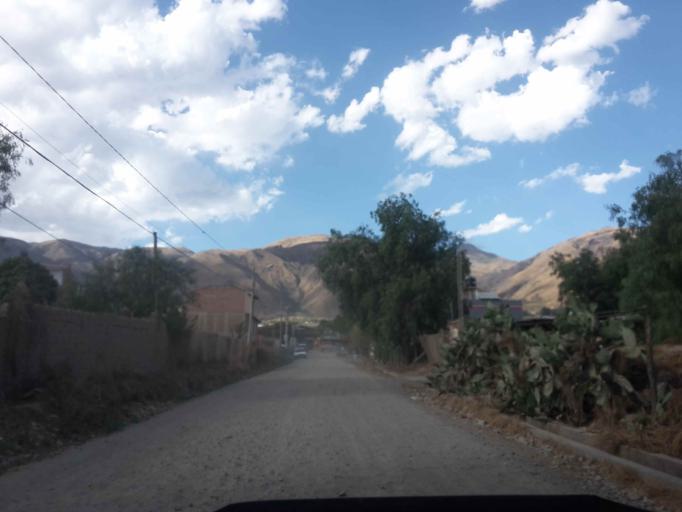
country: BO
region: Cochabamba
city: Cochabamba
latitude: -17.3475
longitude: -66.2027
